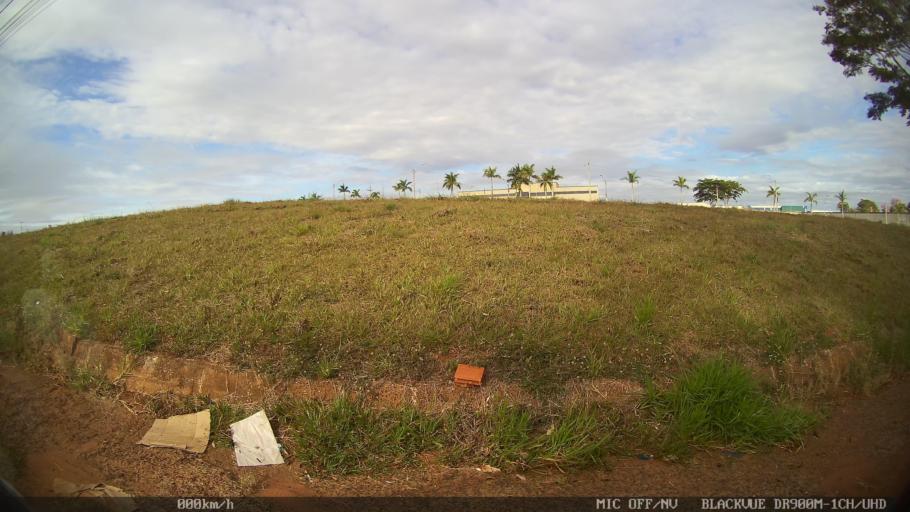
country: BR
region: Sao Paulo
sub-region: Sao Jose Do Rio Preto
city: Sao Jose do Rio Preto
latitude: -20.8238
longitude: -49.4175
